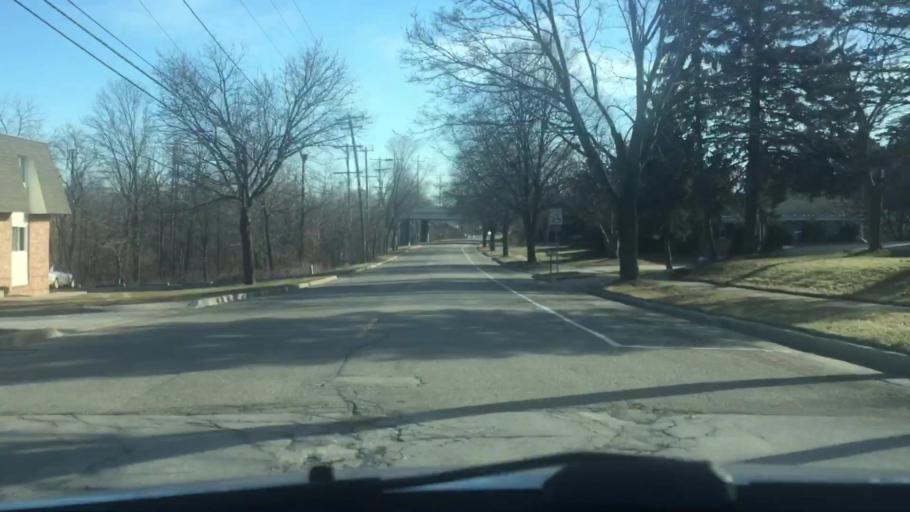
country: US
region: Wisconsin
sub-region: Waukesha County
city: Pewaukee
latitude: 43.0790
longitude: -88.2536
